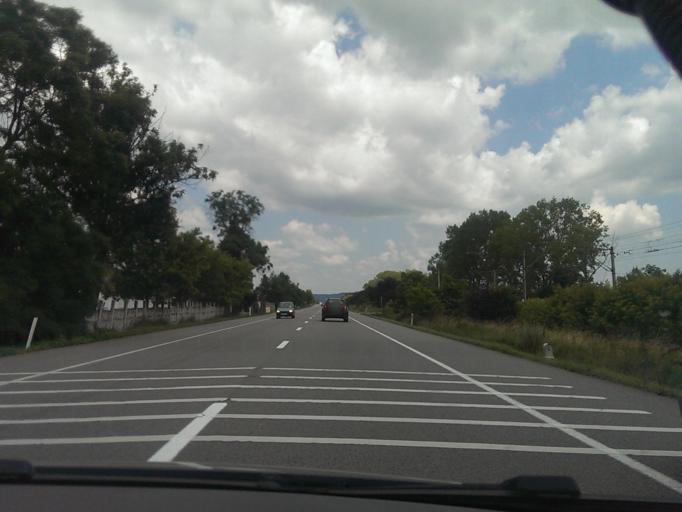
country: RO
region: Cluj
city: Jucu Herghelia
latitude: 46.8677
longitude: 23.7667
